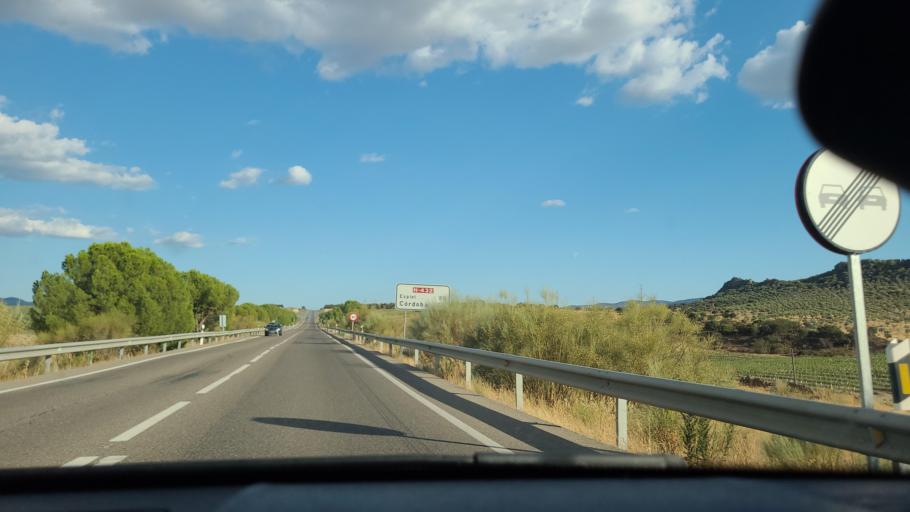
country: ES
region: Andalusia
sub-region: Province of Cordoba
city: Belmez
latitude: 38.2615
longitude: -5.1794
